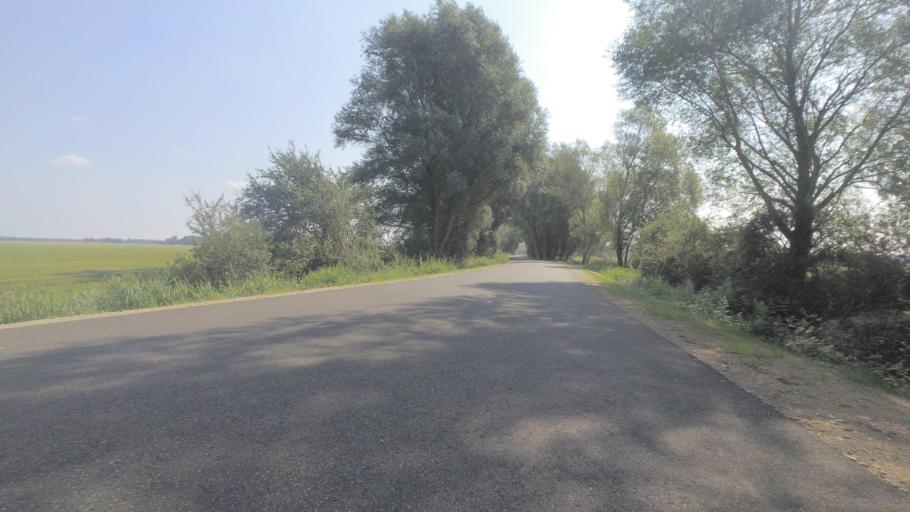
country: DE
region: Mecklenburg-Vorpommern
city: Pampow
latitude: 53.7276
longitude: 12.6720
